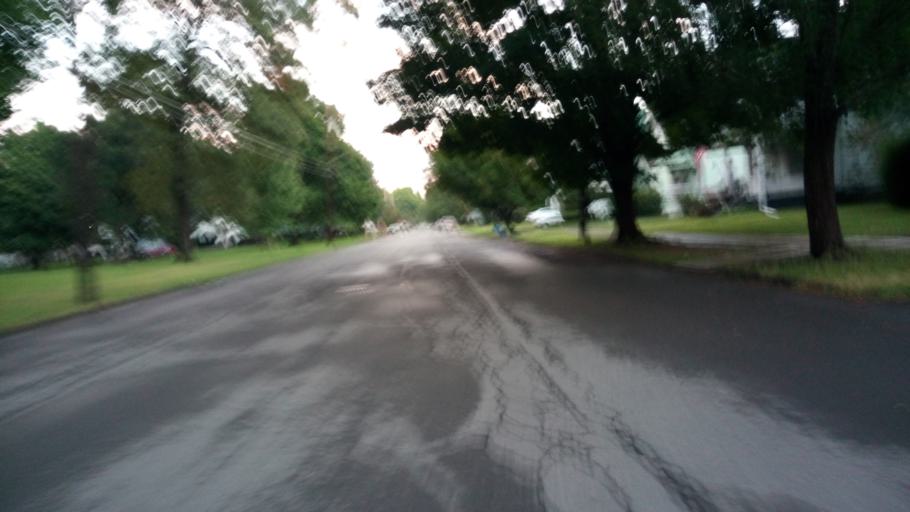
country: US
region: New York
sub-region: Chemung County
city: Elmira
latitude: 42.0924
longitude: -76.8231
